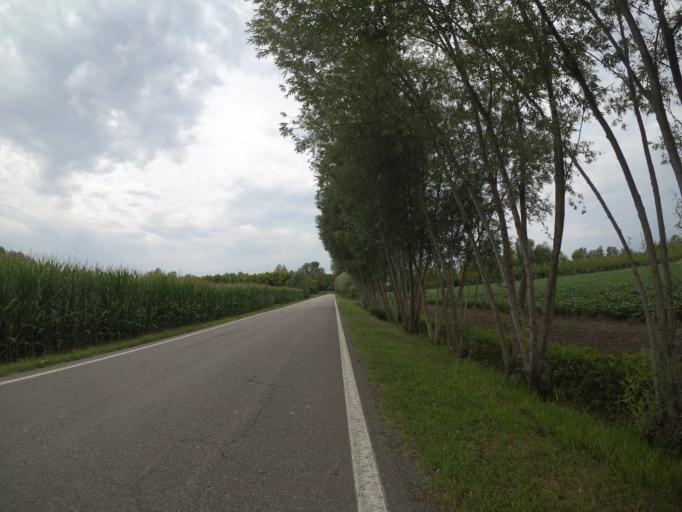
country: IT
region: Friuli Venezia Giulia
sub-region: Provincia di Udine
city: Camino al Tagliamento
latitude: 45.9182
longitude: 12.9619
